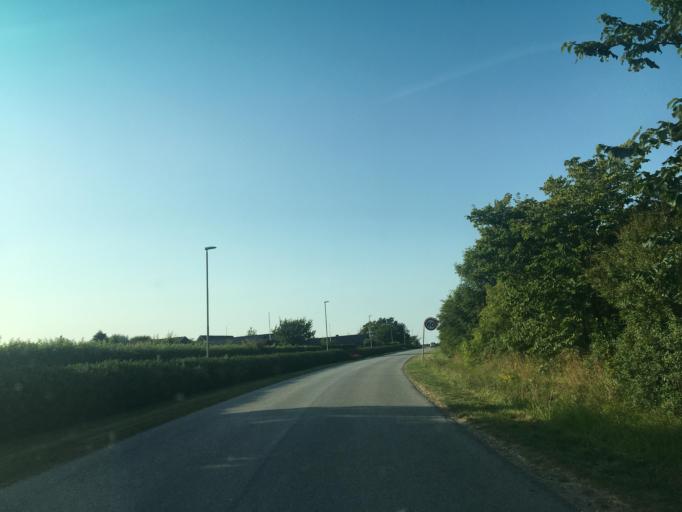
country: DK
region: North Denmark
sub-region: Thisted Kommune
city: Hurup
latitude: 56.7550
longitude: 8.4242
